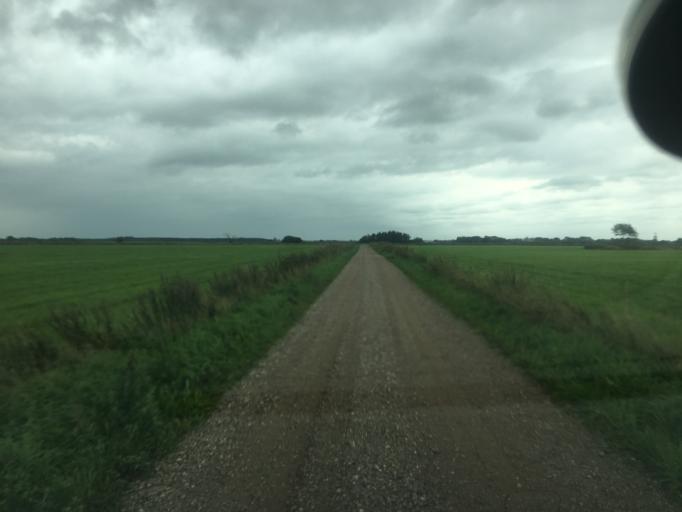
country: DK
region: South Denmark
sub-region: Tonder Kommune
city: Tonder
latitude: 54.9739
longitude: 8.9325
